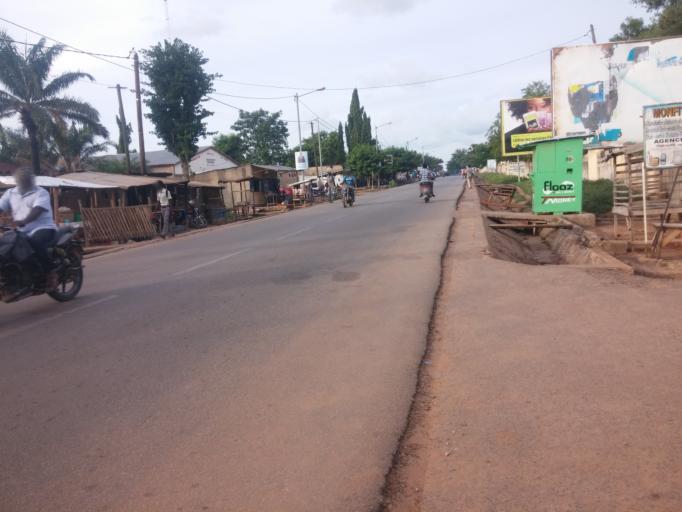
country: TG
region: Kara
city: Kara
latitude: 9.5500
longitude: 1.2003
